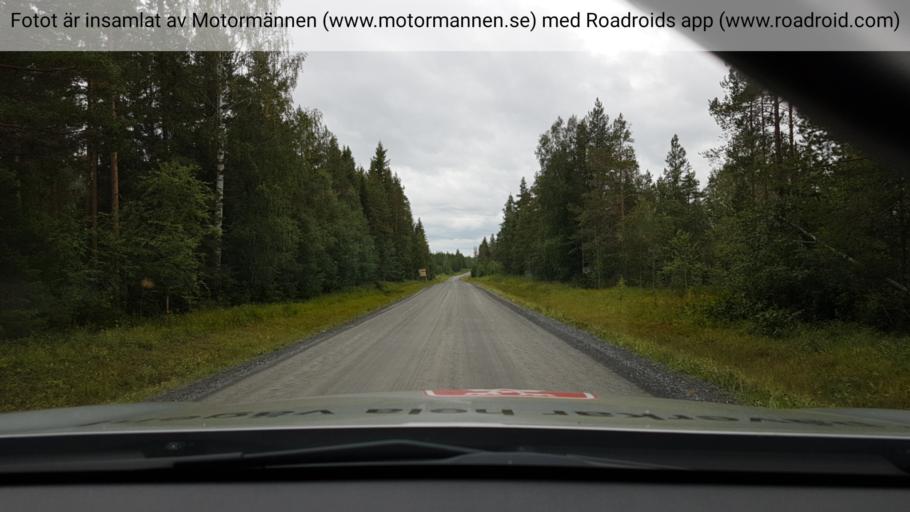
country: SE
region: Vaesterbotten
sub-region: Skelleftea Kommun
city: Forsbacka
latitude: 64.8257
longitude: 20.4975
